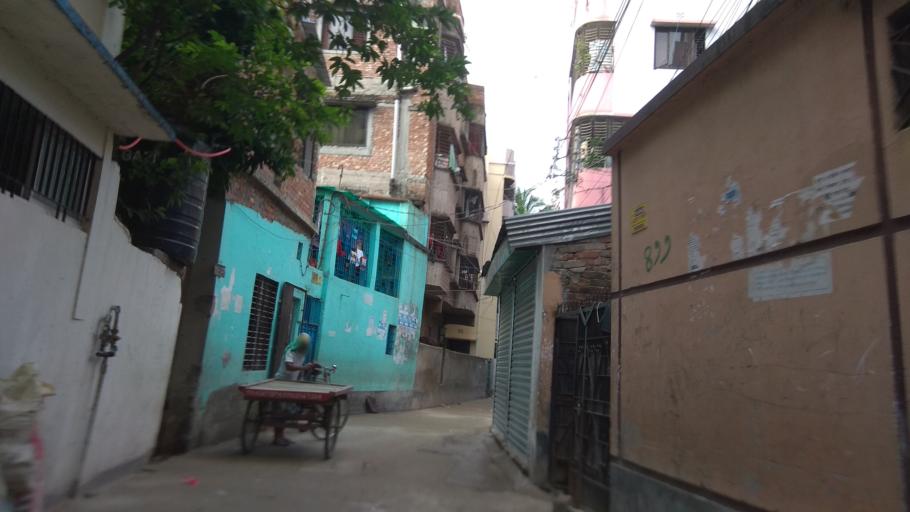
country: BD
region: Dhaka
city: Azimpur
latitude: 23.7932
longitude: 90.3834
